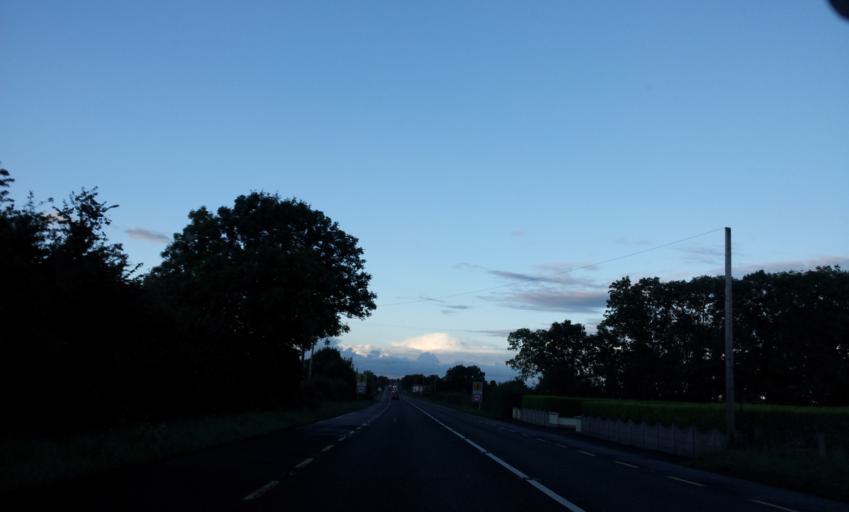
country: IE
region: Munster
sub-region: County Limerick
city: Newcastle West
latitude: 52.4601
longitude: -9.0316
